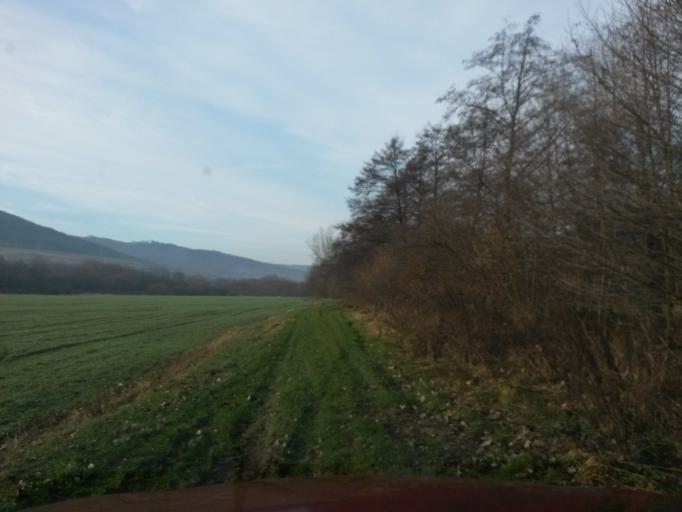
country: SK
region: Kosicky
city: Roznava
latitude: 48.7116
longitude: 20.4597
